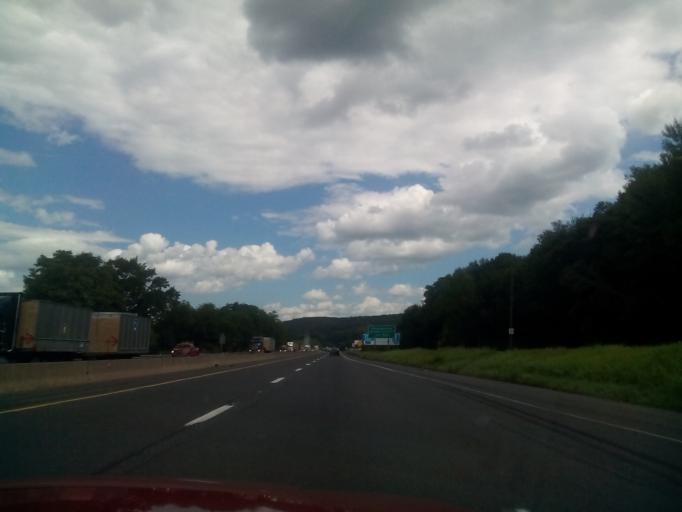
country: US
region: Pennsylvania
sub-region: Monroe County
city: Arlington Heights
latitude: 40.9811
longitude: -75.2106
